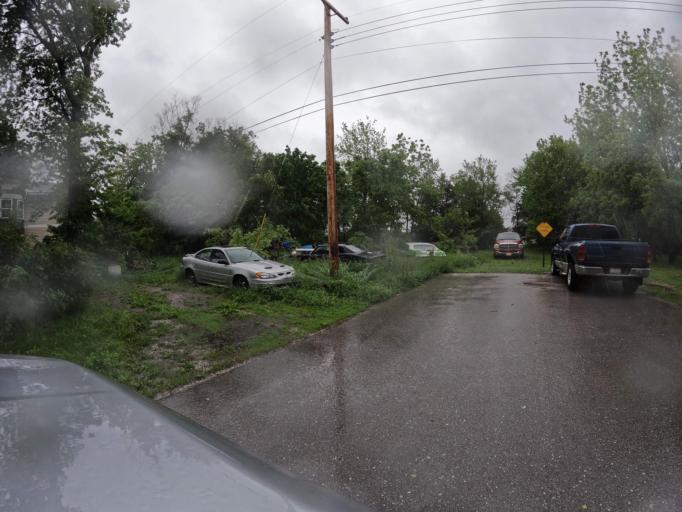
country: US
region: Nebraska
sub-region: Gage County
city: Wymore
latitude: 40.1425
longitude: -96.6668
